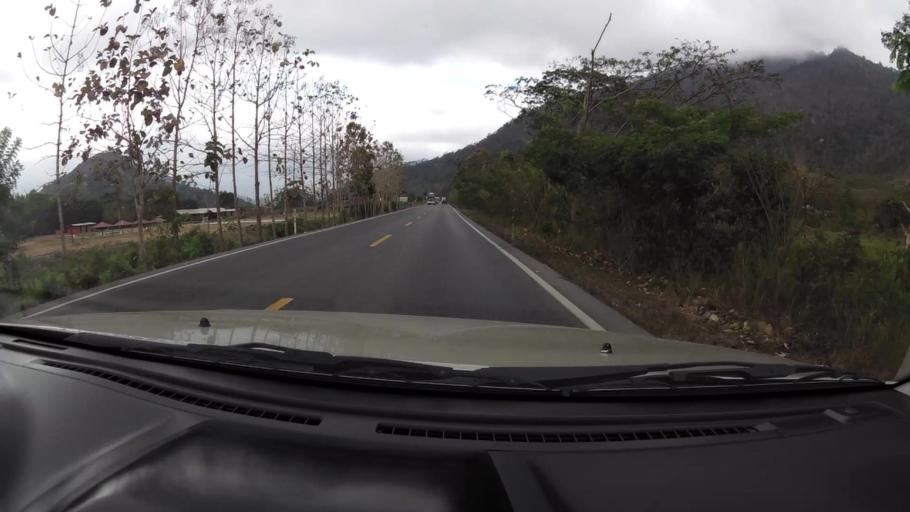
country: EC
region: Guayas
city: Coronel Marcelino Mariduena
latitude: -2.3950
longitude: -79.6301
